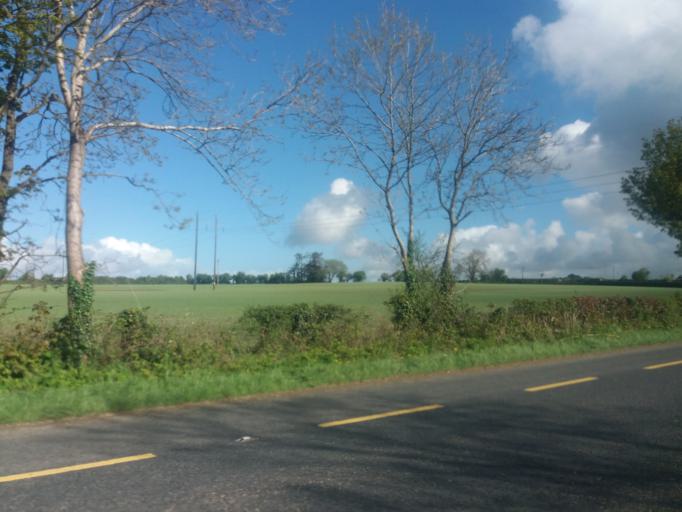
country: IE
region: Leinster
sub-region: Loch Garman
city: Ferns
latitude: 52.5611
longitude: -6.5303
